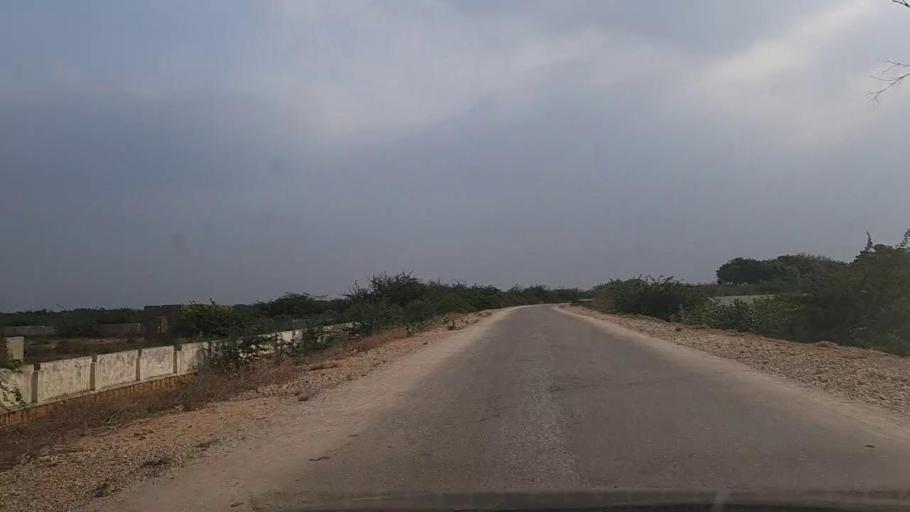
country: PK
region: Sindh
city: Thatta
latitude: 24.8545
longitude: 67.7783
